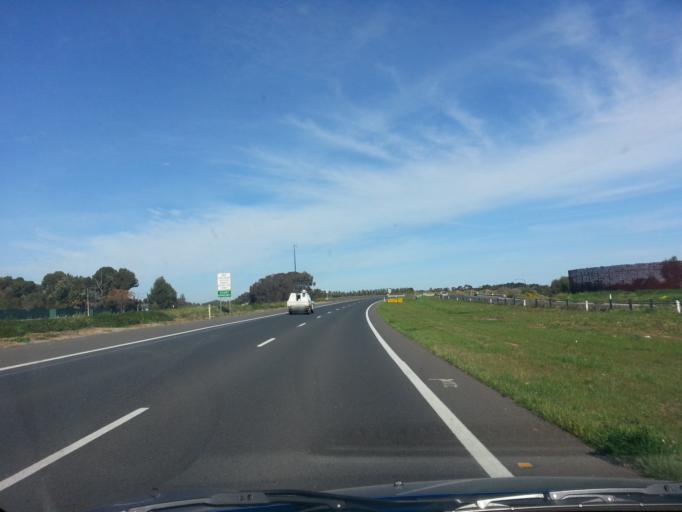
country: AU
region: South Australia
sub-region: Gawler
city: Gawler
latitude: -34.5977
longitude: 138.7281
